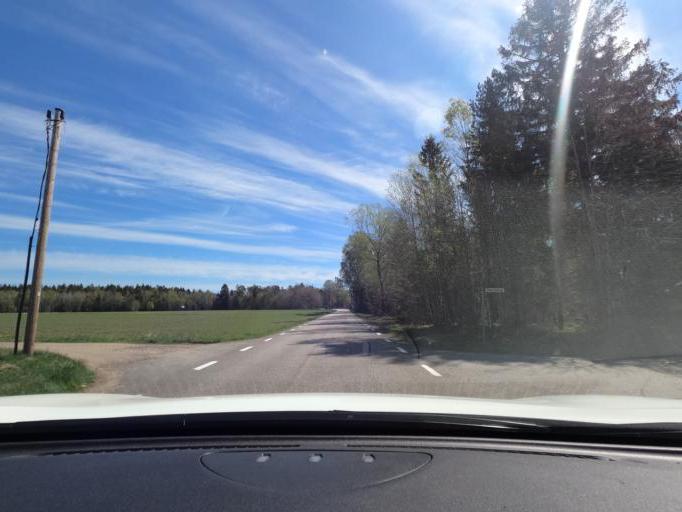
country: SE
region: Vaestra Goetaland
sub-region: Marks Kommun
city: Horred
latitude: 57.4241
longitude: 12.3570
